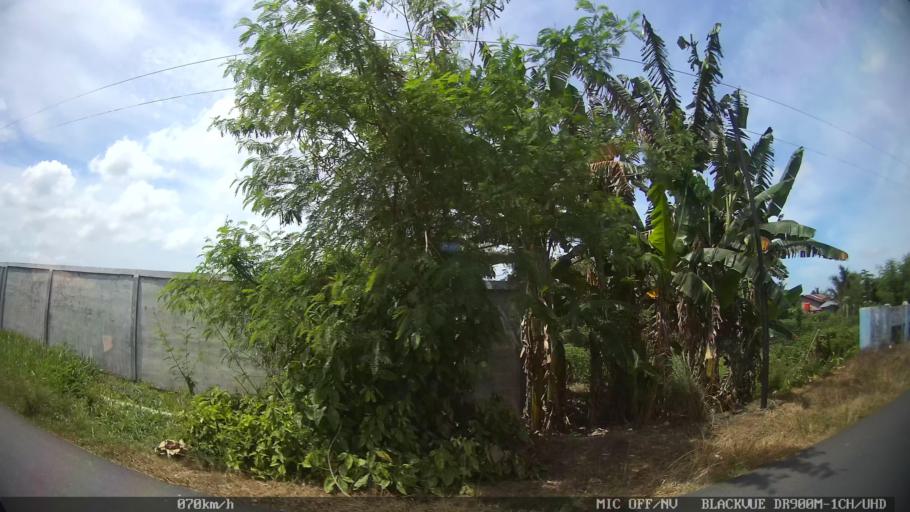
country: ID
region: North Sumatra
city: Percut
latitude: 3.5892
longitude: 98.8789
